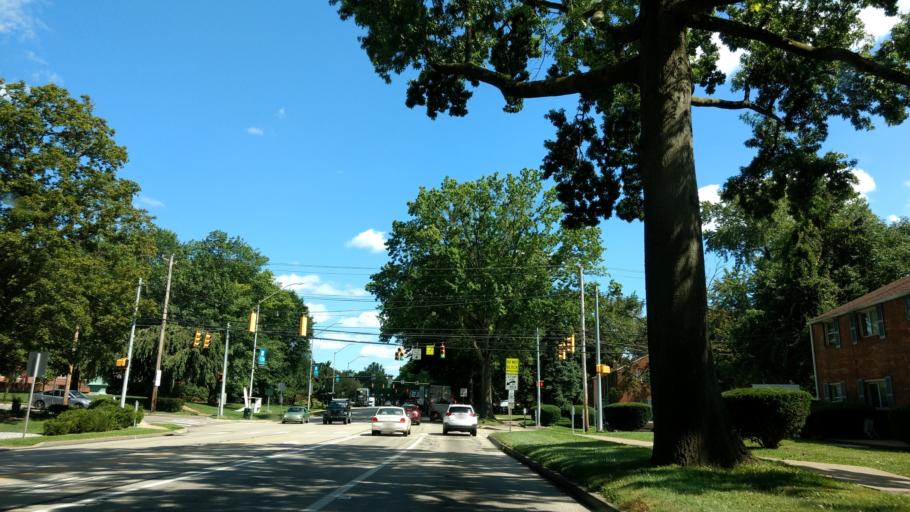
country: US
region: Pennsylvania
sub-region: Allegheny County
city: Sewickley
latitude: 40.5376
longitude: -80.1866
